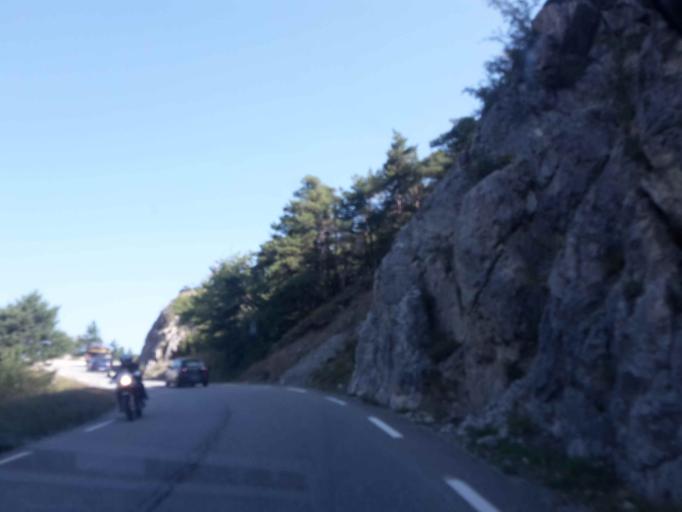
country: FR
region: Provence-Alpes-Cote d'Azur
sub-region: Departement des Hautes-Alpes
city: Guillestre
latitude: 44.6417
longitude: 6.6628
